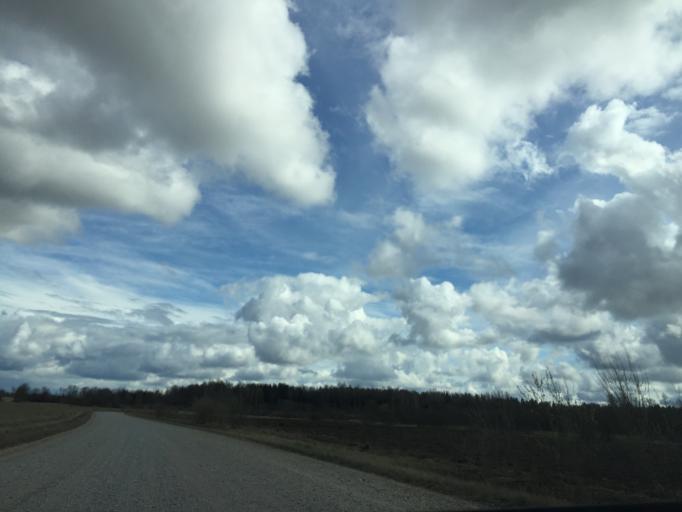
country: LV
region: Limbazu Rajons
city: Limbazi
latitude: 57.6118
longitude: 24.7821
